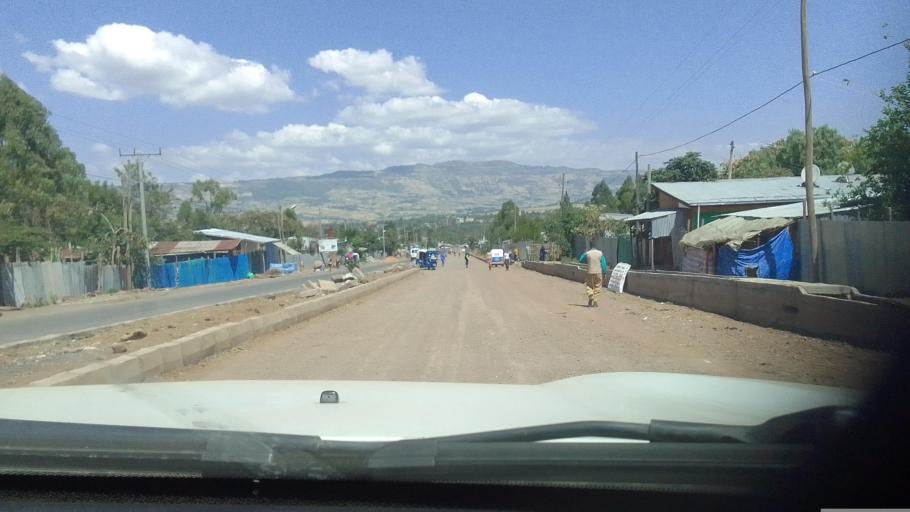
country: ET
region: Oromiya
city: Hagere Hiywet
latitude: 8.9687
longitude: 37.8484
